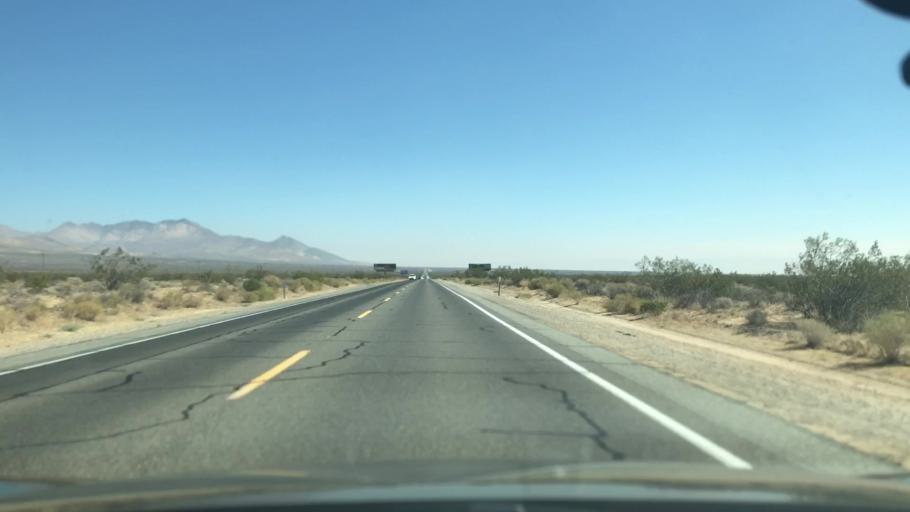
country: US
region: California
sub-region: Kern County
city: Inyokern
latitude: 35.4945
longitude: -117.9517
